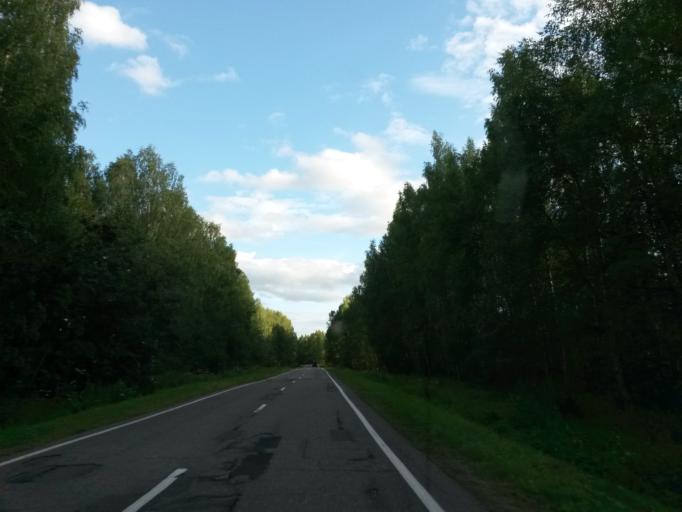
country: RU
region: Jaroslavl
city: Tutayev
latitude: 57.9168
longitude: 39.5154
